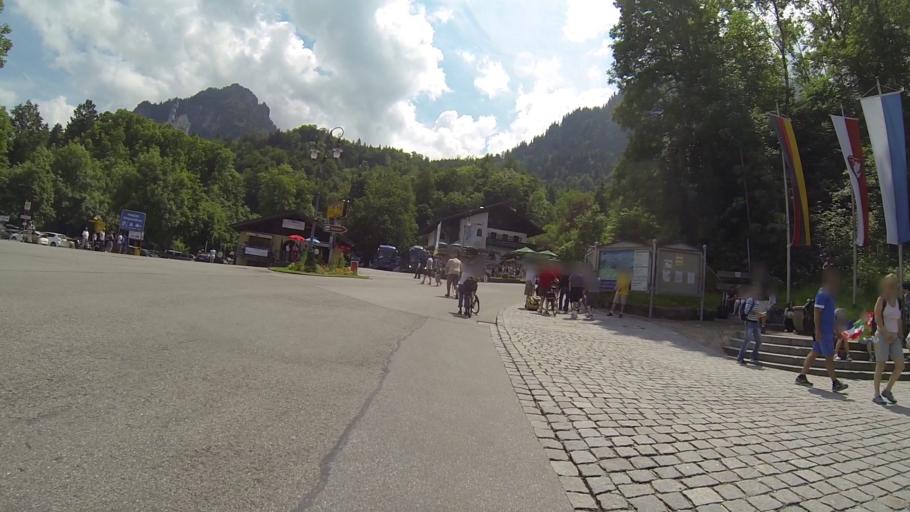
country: DE
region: Bavaria
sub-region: Swabia
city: Schwangau
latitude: 47.5567
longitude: 10.7403
